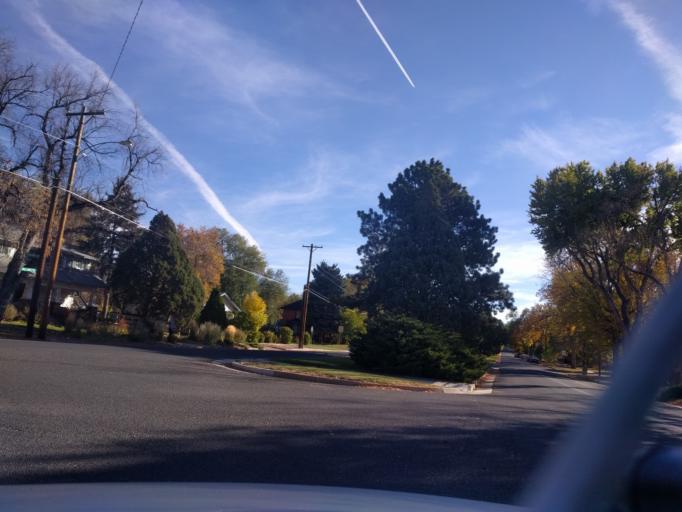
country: US
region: Colorado
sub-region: El Paso County
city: Colorado Springs
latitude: 38.8421
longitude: -104.8161
